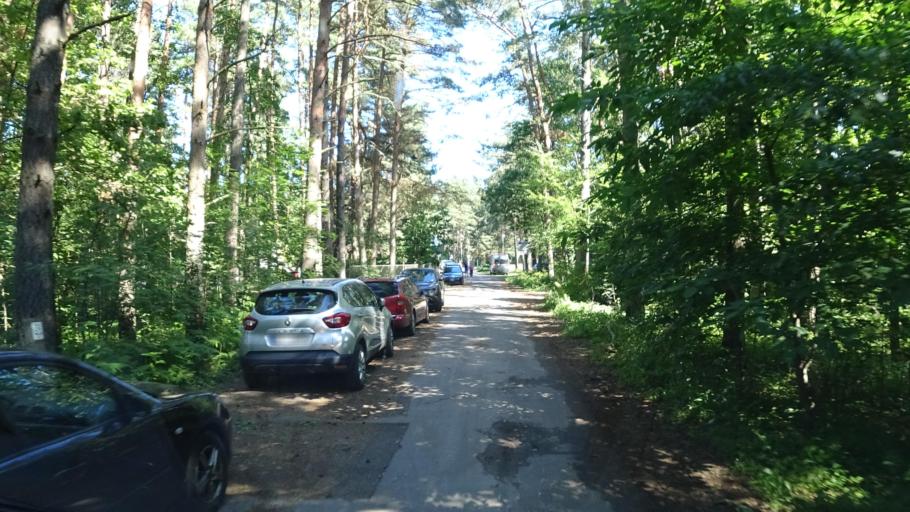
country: LV
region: Jurmala
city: Jurmala
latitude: 56.9588
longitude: 23.6428
